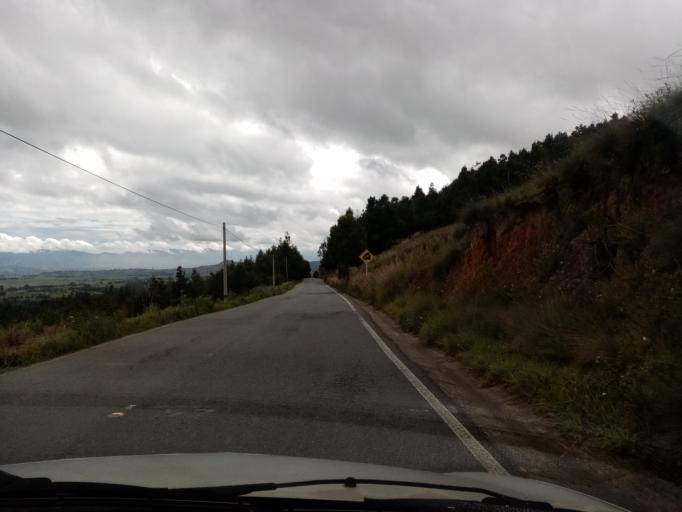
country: CO
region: Boyaca
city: Siachoque
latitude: 5.5725
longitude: -73.2731
